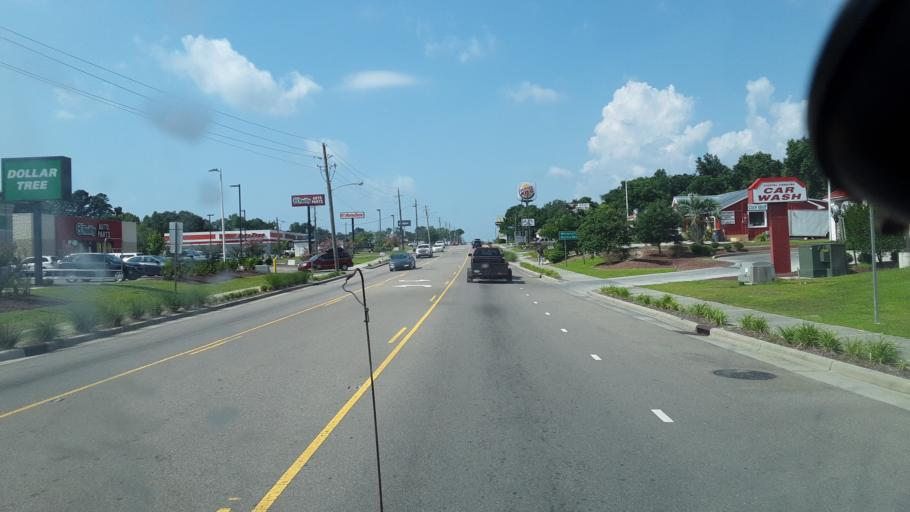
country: US
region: North Carolina
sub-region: Brunswick County
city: Shallotte
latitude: 33.9786
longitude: -78.3777
